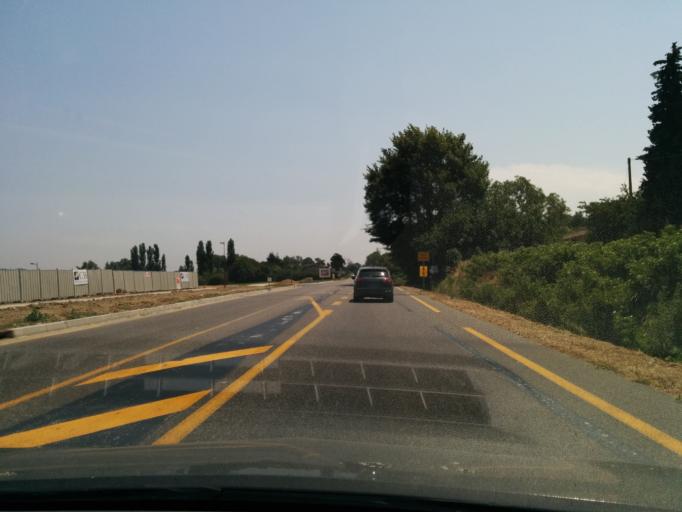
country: FR
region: Midi-Pyrenees
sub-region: Departement de la Haute-Garonne
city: Pompertuzat
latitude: 43.4990
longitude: 1.5157
